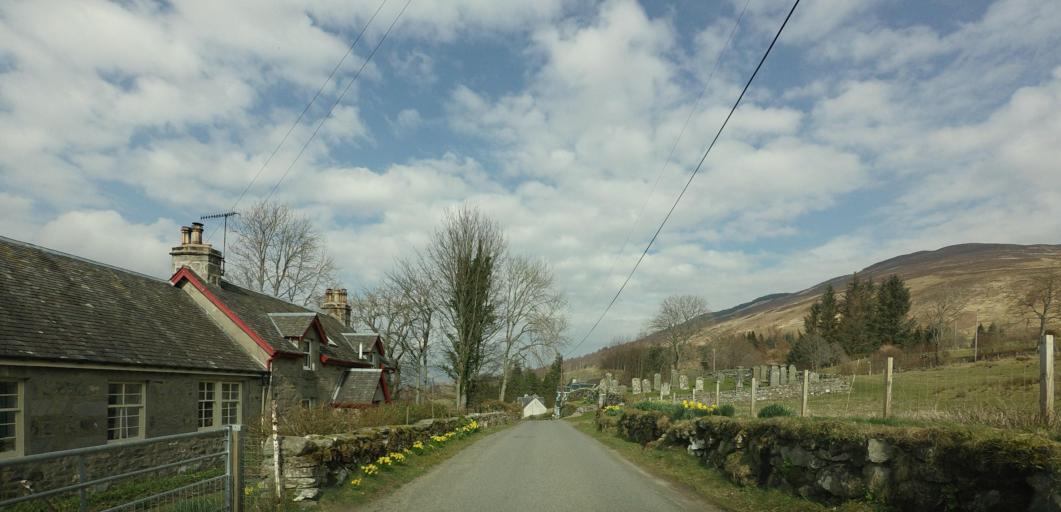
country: GB
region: Scotland
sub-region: Perth and Kinross
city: Comrie
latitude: 56.5262
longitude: -4.1125
